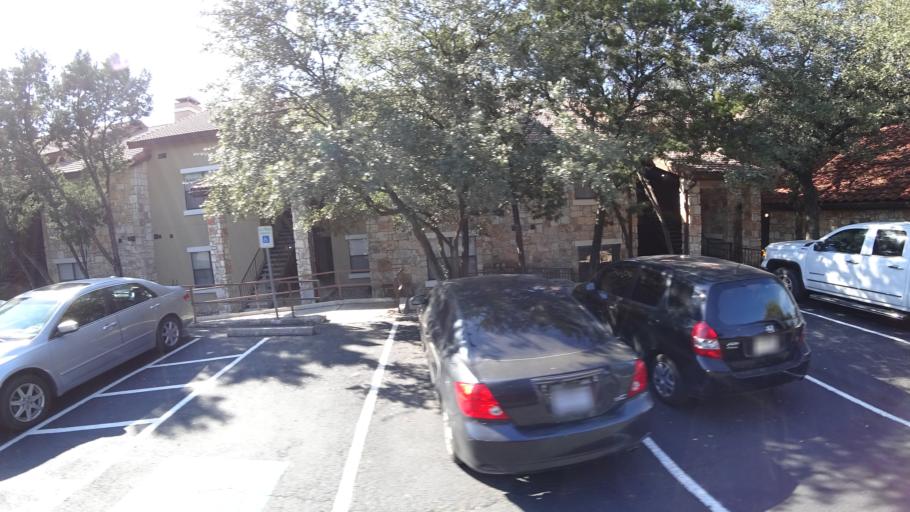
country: US
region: Texas
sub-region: Williamson County
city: Jollyville
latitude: 30.3728
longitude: -97.7623
